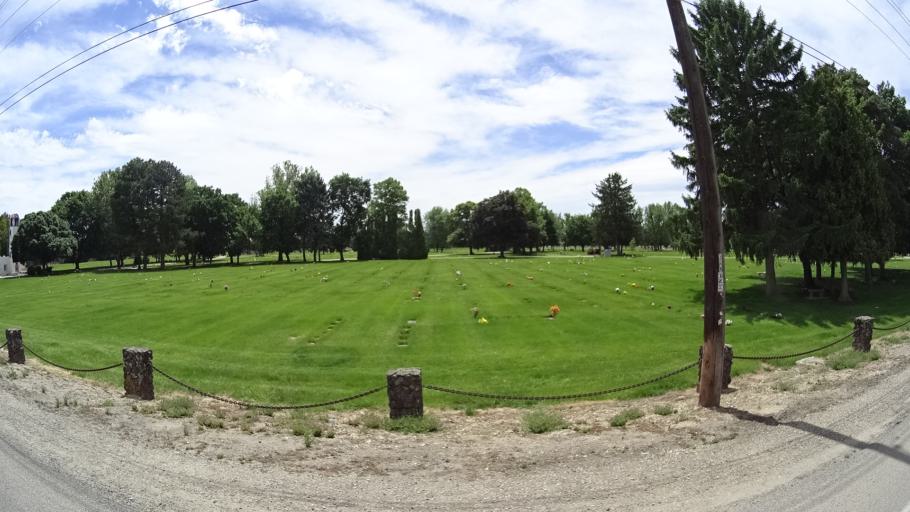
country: US
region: Idaho
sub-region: Ada County
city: Meridian
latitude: 43.6194
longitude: -116.3317
